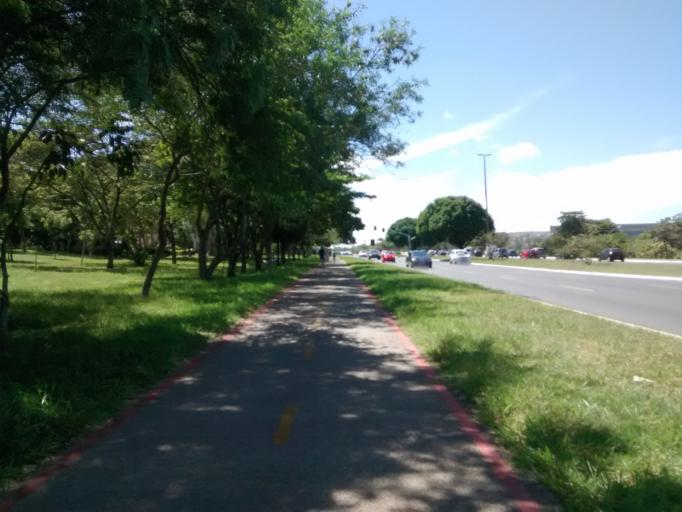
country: BR
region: Federal District
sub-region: Brasilia
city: Brasilia
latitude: -15.8173
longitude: -47.8912
